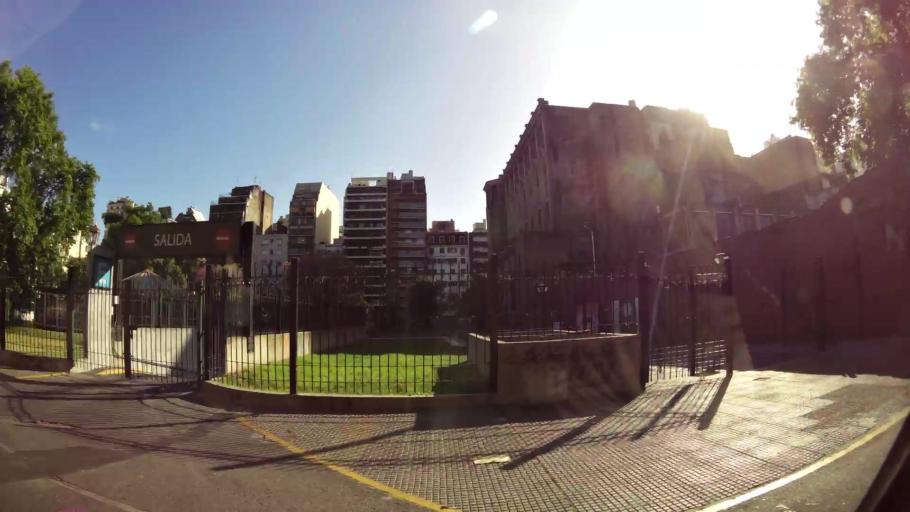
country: AR
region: Buenos Aires F.D.
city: Retiro
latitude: -34.5885
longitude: -58.3973
